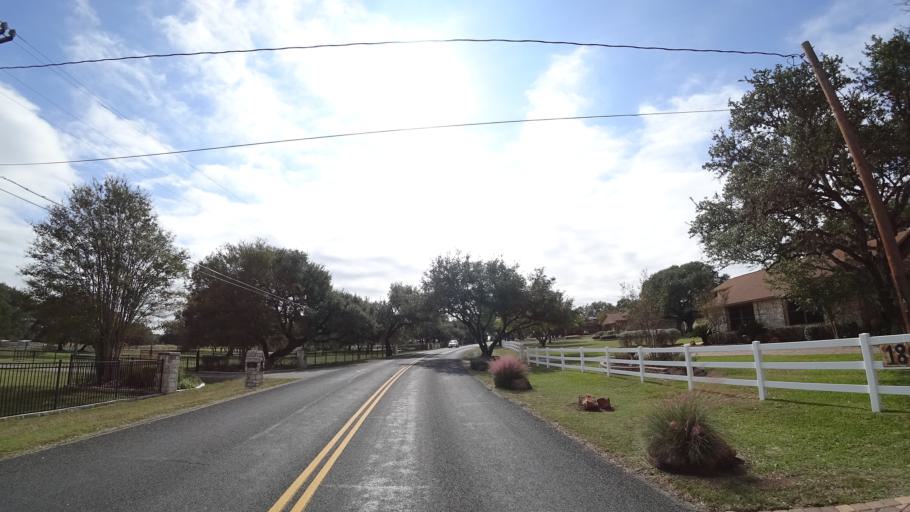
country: US
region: Texas
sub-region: Williamson County
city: Brushy Creek
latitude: 30.5280
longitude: -97.7368
